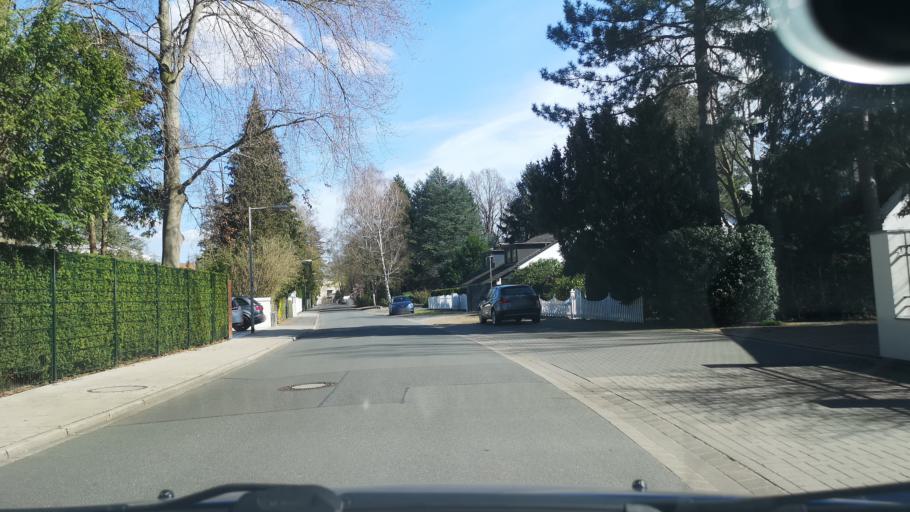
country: DE
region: Lower Saxony
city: Isernhagen Farster Bauerschaft
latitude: 52.4361
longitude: 9.7987
